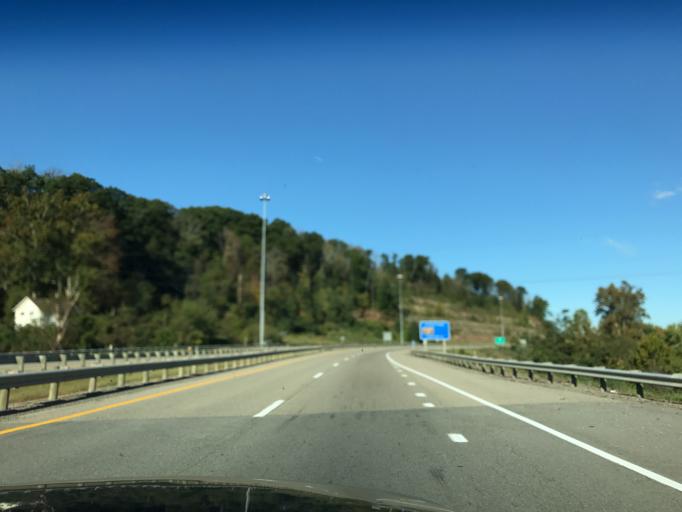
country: US
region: West Virginia
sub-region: Wood County
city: Parkersburg
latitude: 39.2594
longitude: -81.5617
